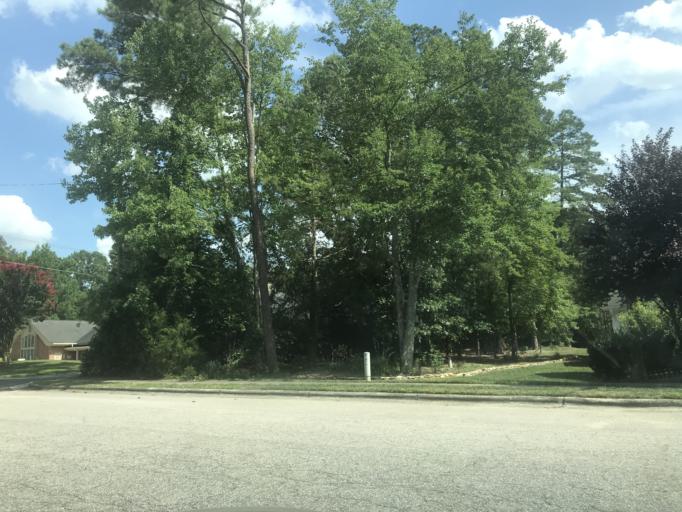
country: US
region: North Carolina
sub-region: Wake County
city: West Raleigh
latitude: 35.8676
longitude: -78.7088
